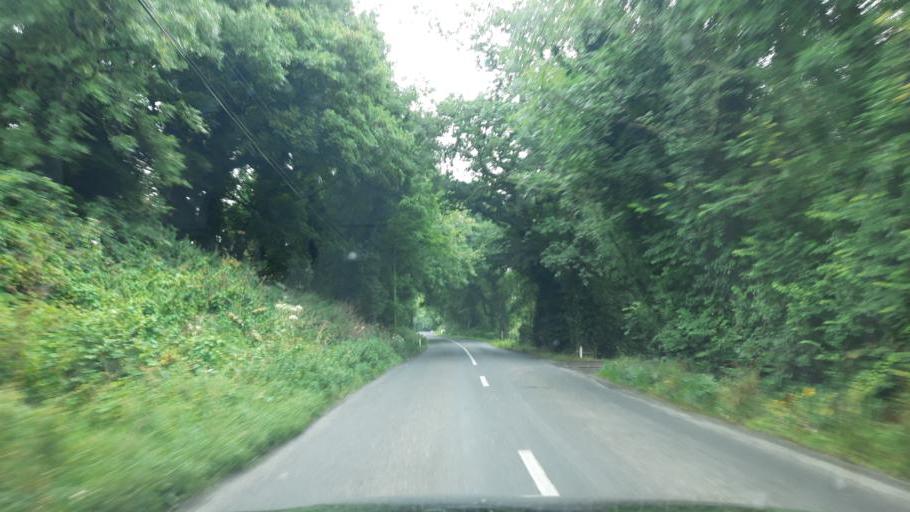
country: IE
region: Munster
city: Fethard
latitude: 52.5410
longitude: -7.6816
